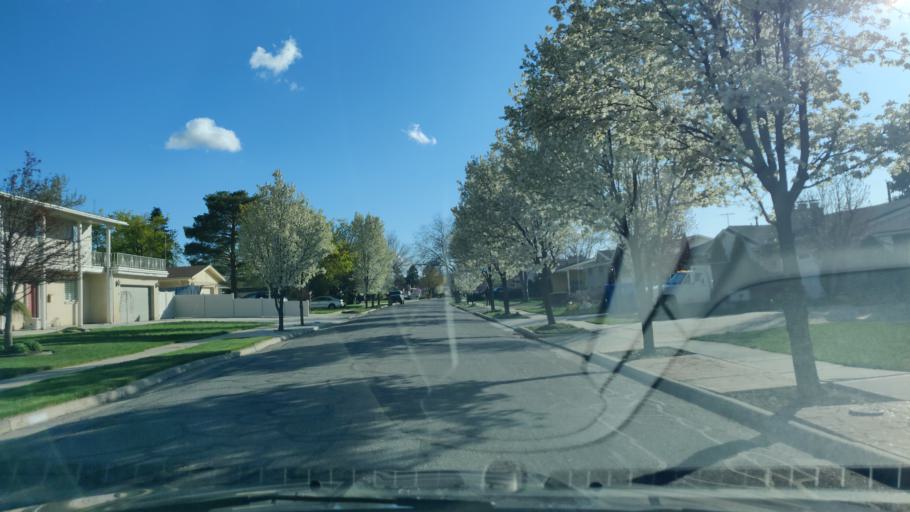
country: US
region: Utah
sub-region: Salt Lake County
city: Cottonwood Heights
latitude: 40.6188
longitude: -111.8204
